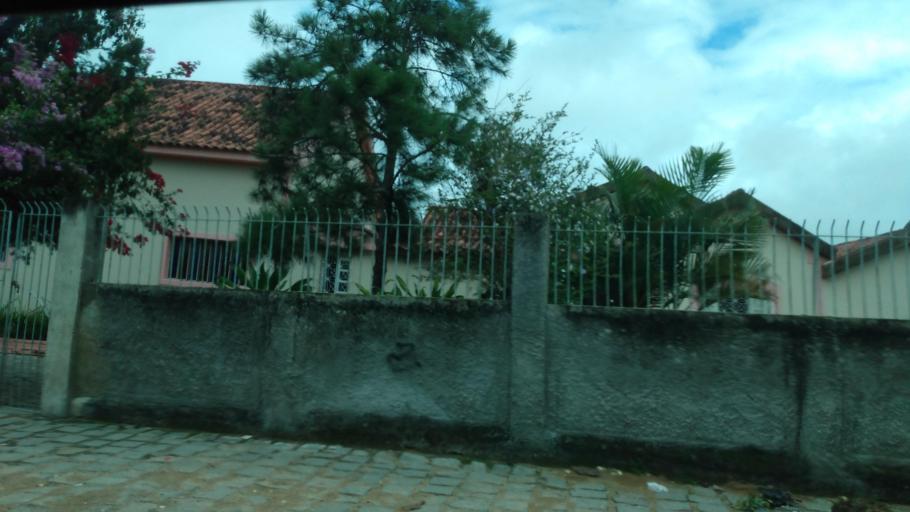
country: BR
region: Pernambuco
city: Garanhuns
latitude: -8.8826
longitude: -36.4817
